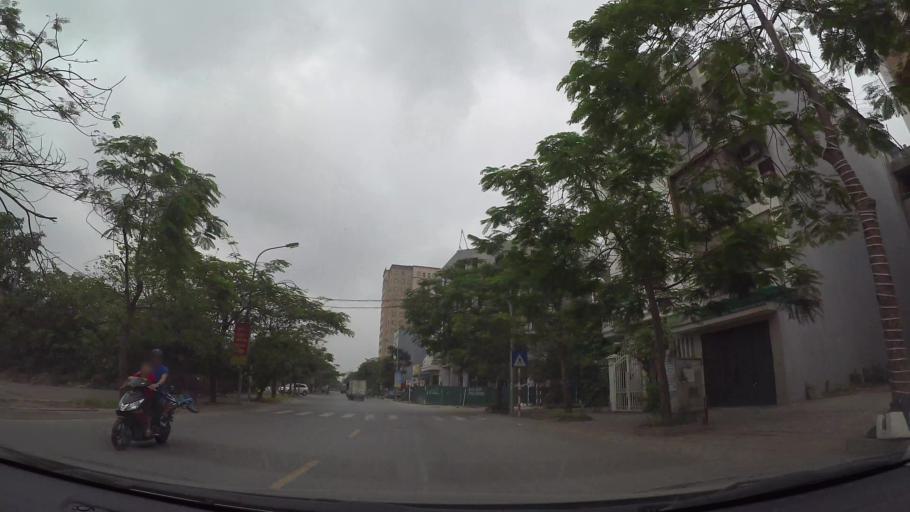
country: VN
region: Ha Noi
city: Trau Quy
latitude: 21.0580
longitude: 105.9161
